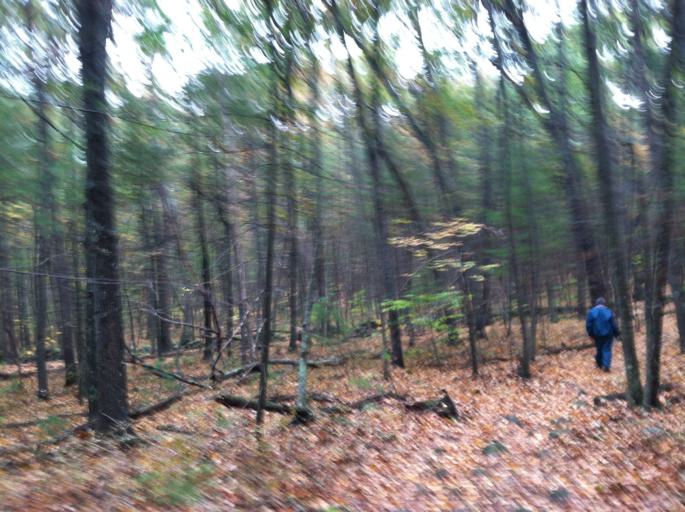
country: US
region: Massachusetts
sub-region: Middlesex County
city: Carlisle
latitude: 42.4957
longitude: -71.3583
